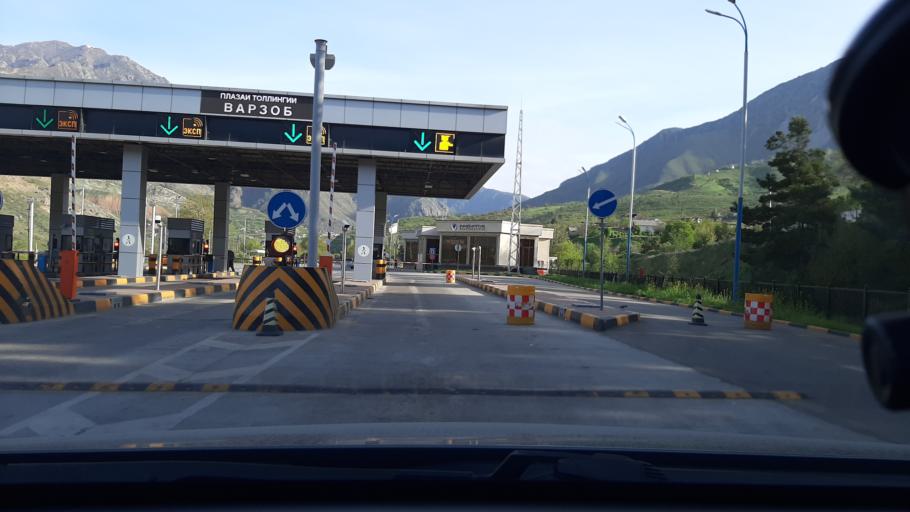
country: TJ
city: Varzob
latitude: 38.6830
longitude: 68.7916
